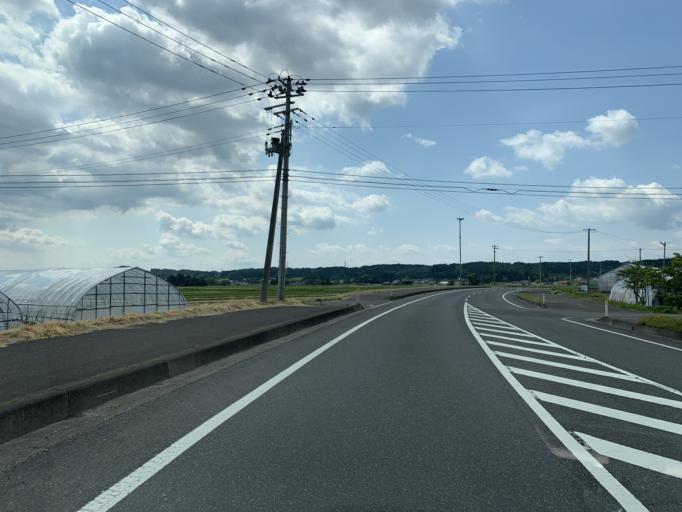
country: JP
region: Miyagi
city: Furukawa
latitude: 38.7406
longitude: 140.9598
